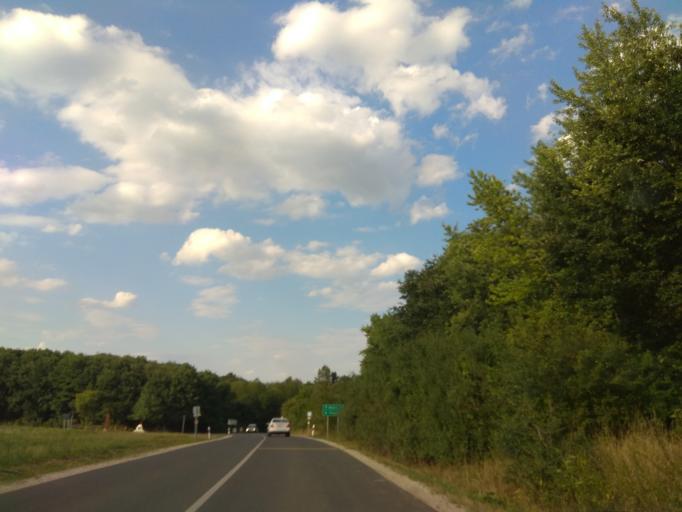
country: HU
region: Borsod-Abauj-Zemplen
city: Harsany
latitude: 47.9885
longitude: 20.7512
